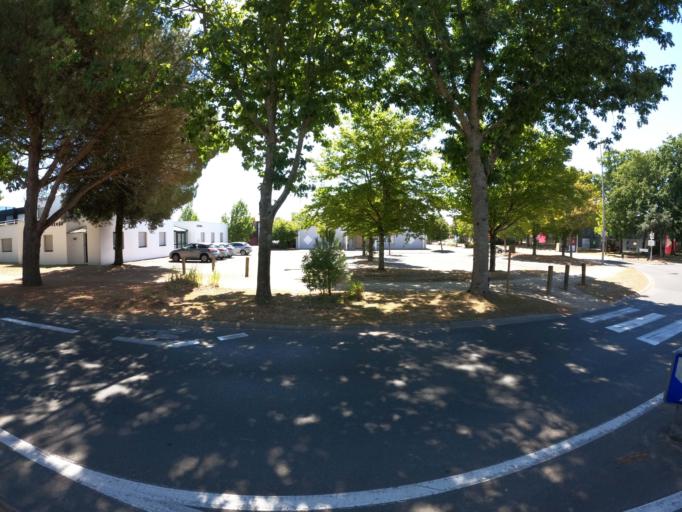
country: FR
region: Pays de la Loire
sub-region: Departement de la Vendee
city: Challans
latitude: 46.8367
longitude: -1.8798
